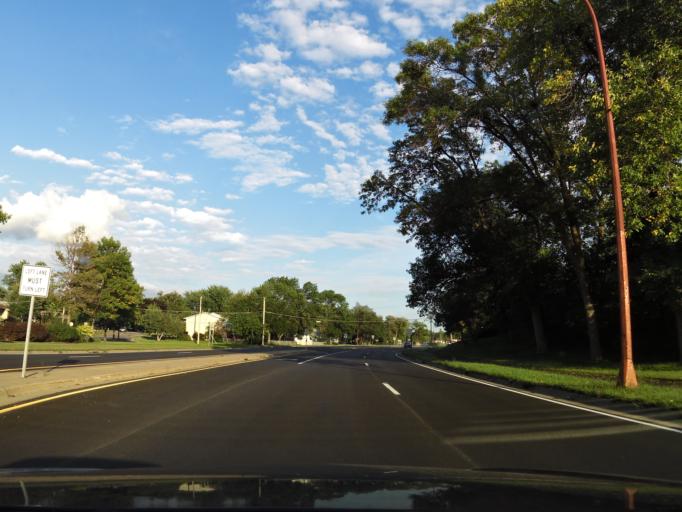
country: US
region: Minnesota
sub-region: Dakota County
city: Hastings
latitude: 44.7382
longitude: -92.8616
